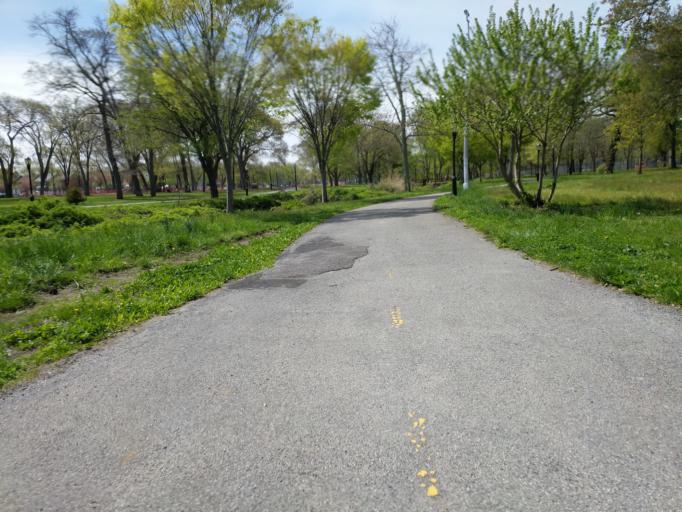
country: US
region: New York
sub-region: Nassau County
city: South Valley Stream
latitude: 40.6628
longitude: -73.7429
